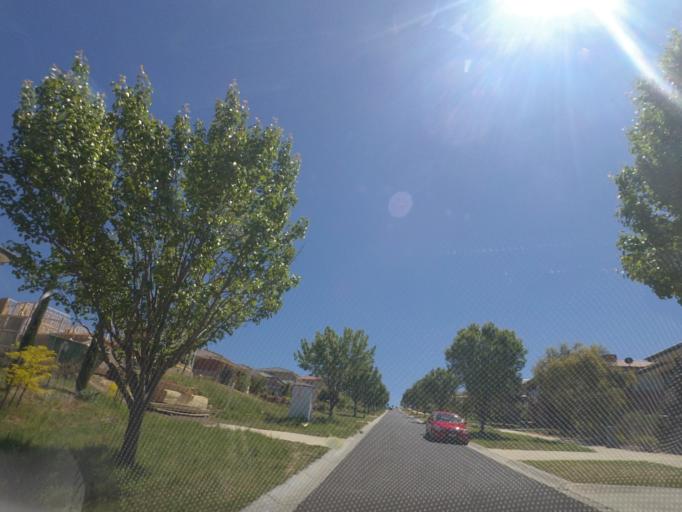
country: AU
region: Victoria
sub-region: Hume
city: Sunbury
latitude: -37.5564
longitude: 144.7061
